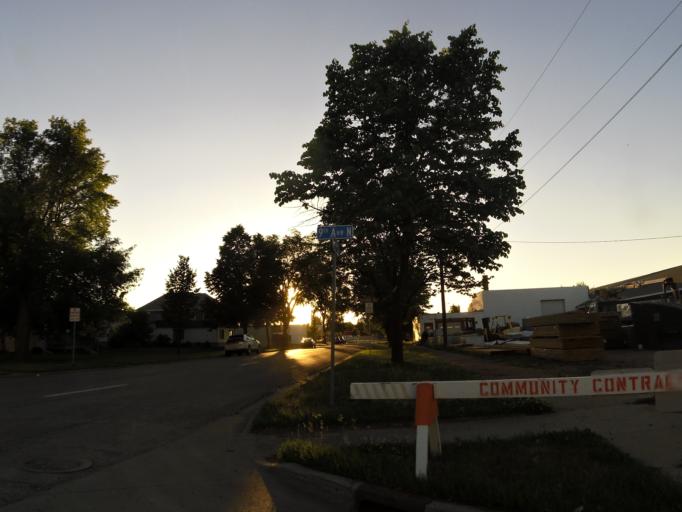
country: US
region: North Dakota
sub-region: Grand Forks County
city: Grand Forks
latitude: 47.9319
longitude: -97.0419
